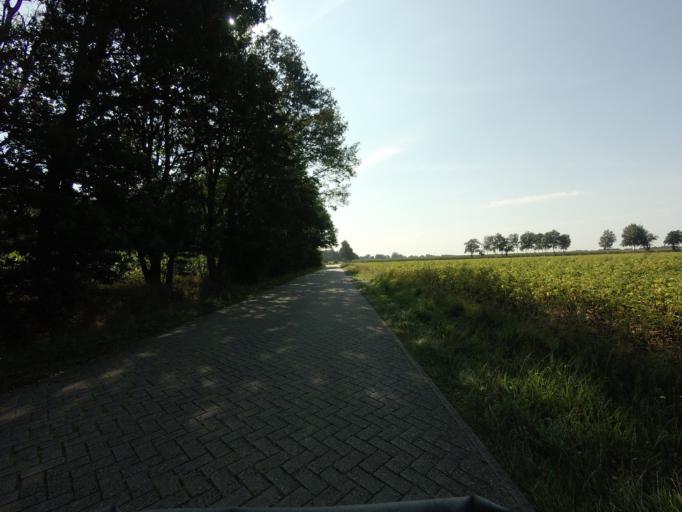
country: DE
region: Lower Saxony
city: Emlichheim
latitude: 52.5963
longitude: 6.8329
